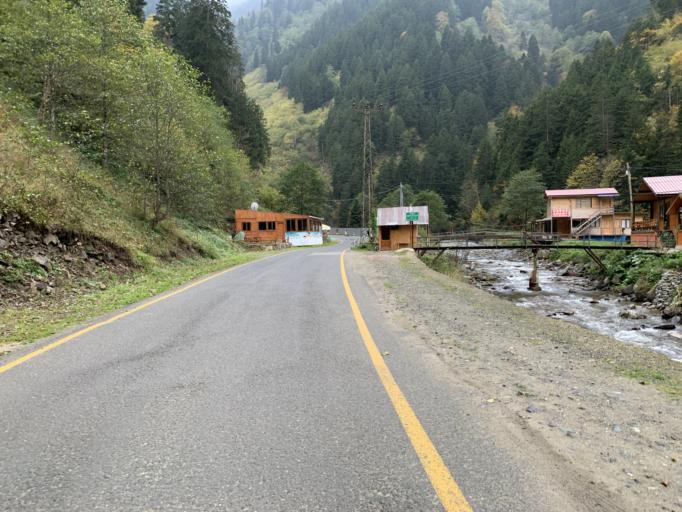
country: TR
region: Trabzon
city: Uzungol
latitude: 40.5958
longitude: 40.3214
